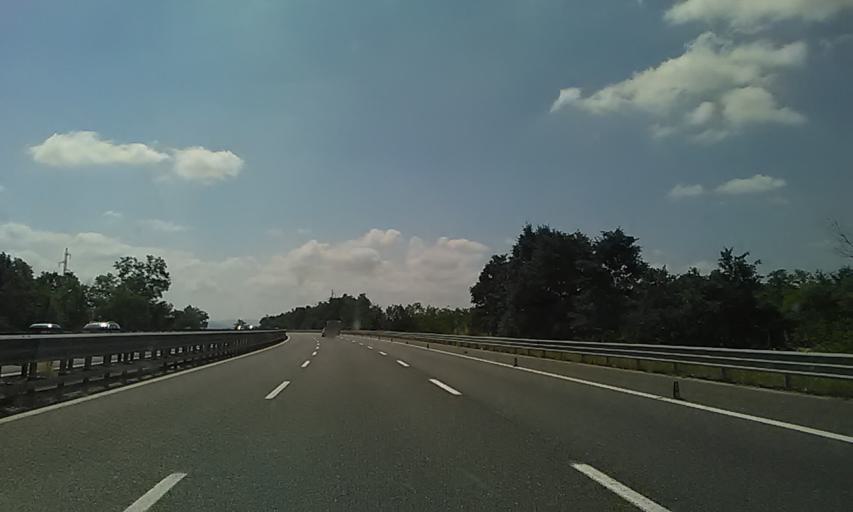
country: IT
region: Piedmont
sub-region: Provincia di Alessandria
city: Predosa
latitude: 44.7403
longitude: 8.6518
